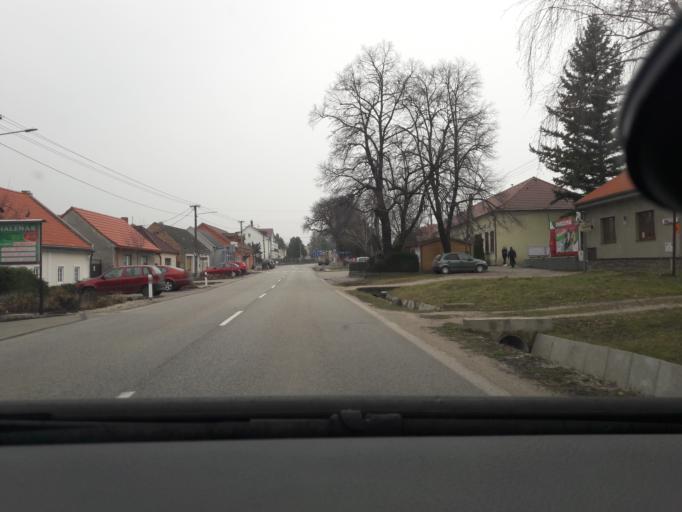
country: SK
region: Trnavsky
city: Smolenice
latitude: 48.5072
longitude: 17.4312
